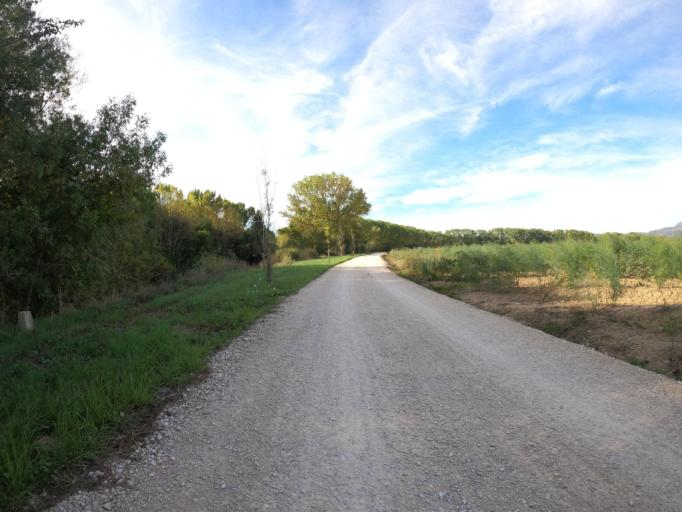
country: ES
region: Navarre
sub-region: Provincia de Navarra
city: Orkoien
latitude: 42.8124
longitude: -1.7294
